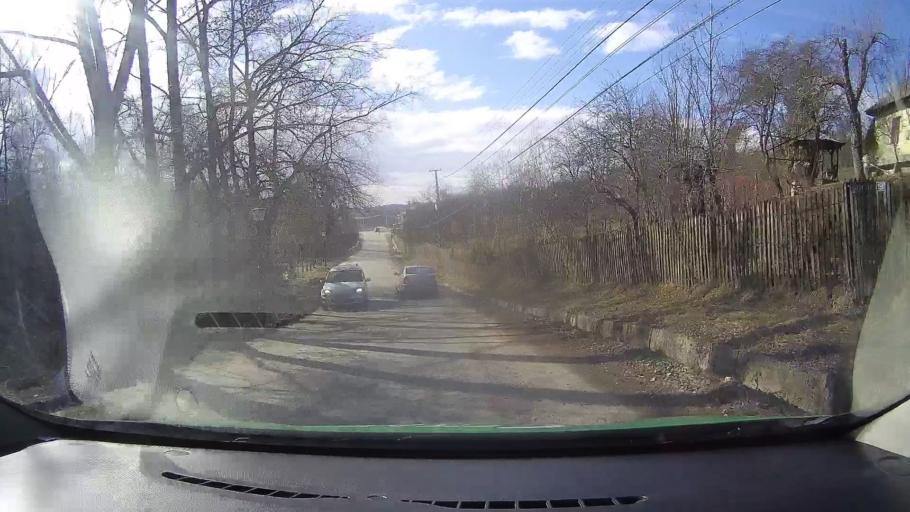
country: RO
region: Dambovita
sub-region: Comuna Varfuri
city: Varfuri
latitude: 45.0963
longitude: 25.5080
